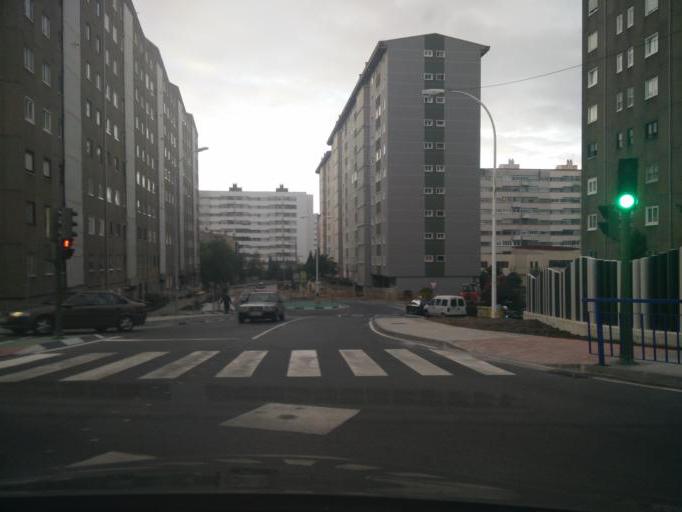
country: ES
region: Galicia
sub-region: Provincia da Coruna
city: A Coruna
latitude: 43.3437
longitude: -8.4137
